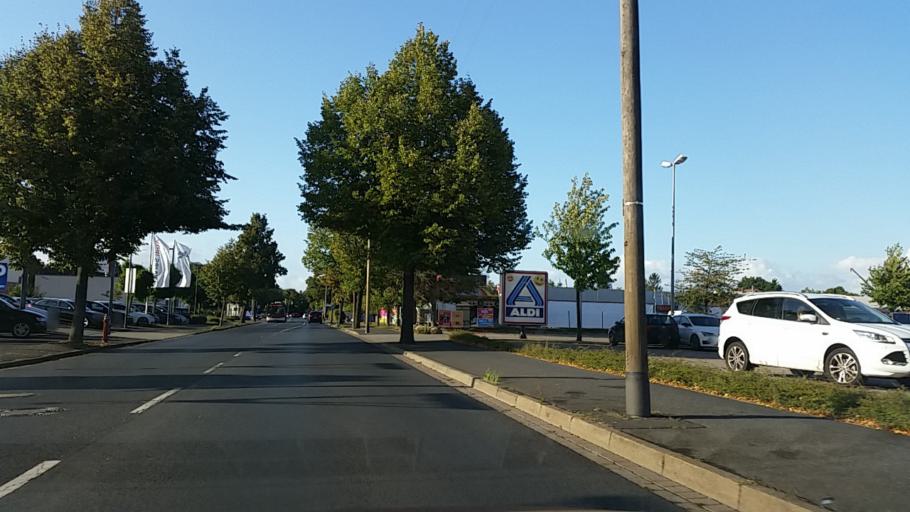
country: DE
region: Lower Saxony
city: Braunschweig
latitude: 52.2883
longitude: 10.5627
